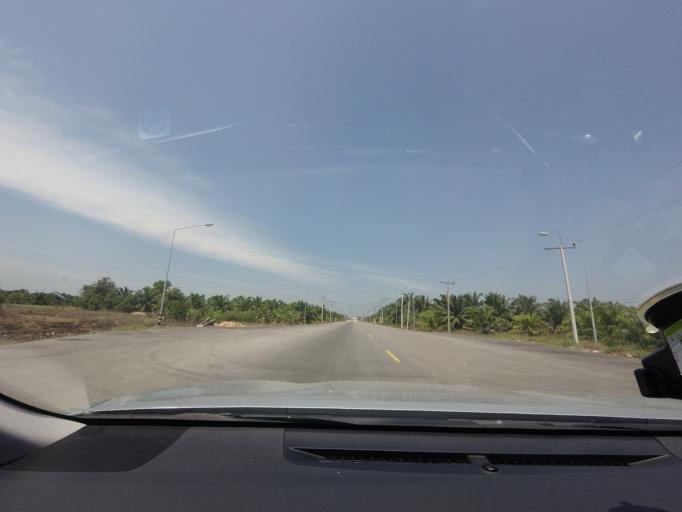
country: TH
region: Surat Thani
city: Tha Chang
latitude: 9.2194
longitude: 99.1786
